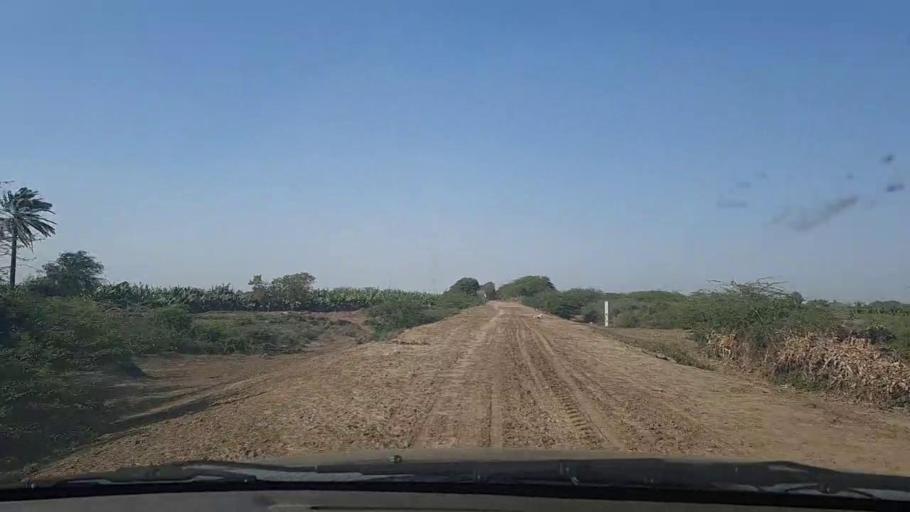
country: PK
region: Sindh
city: Chuhar Jamali
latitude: 24.3314
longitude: 67.7545
